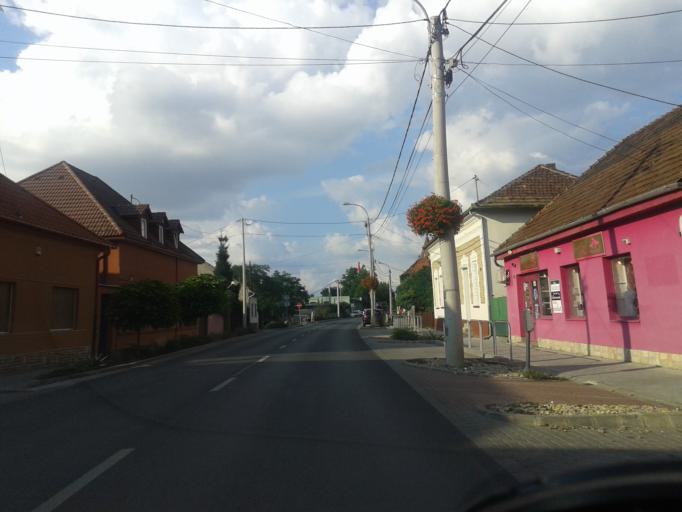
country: HU
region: Pest
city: Dunaharaszti
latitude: 47.3573
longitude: 19.0851
